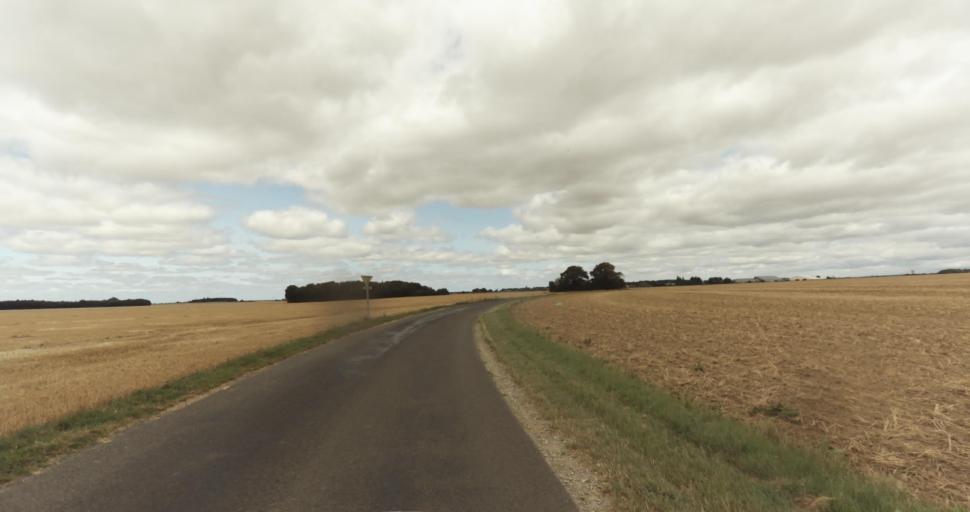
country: FR
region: Haute-Normandie
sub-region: Departement de l'Eure
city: Marcilly-sur-Eure
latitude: 48.9119
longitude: 1.2407
